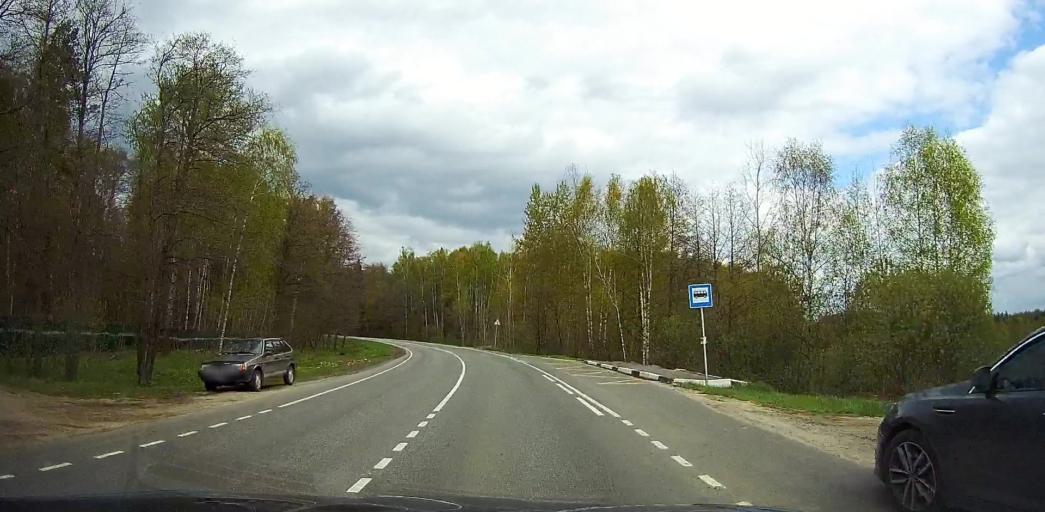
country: RU
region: Moskovskaya
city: Ashitkovo
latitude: 55.4772
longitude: 38.6143
